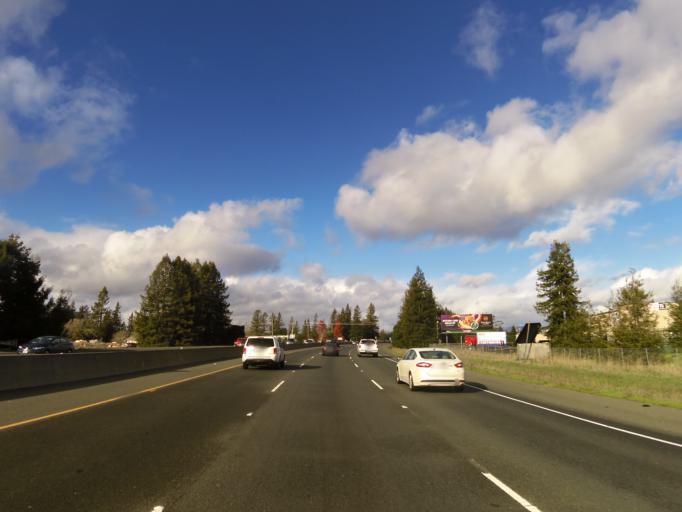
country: US
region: California
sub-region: Sonoma County
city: Rohnert Park
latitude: 38.3742
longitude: -122.7157
